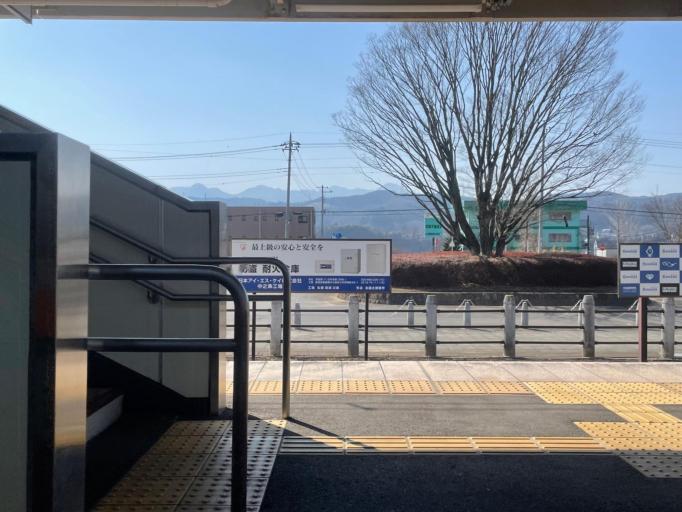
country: JP
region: Gunma
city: Nakanojomachi
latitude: 36.5854
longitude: 138.8511
